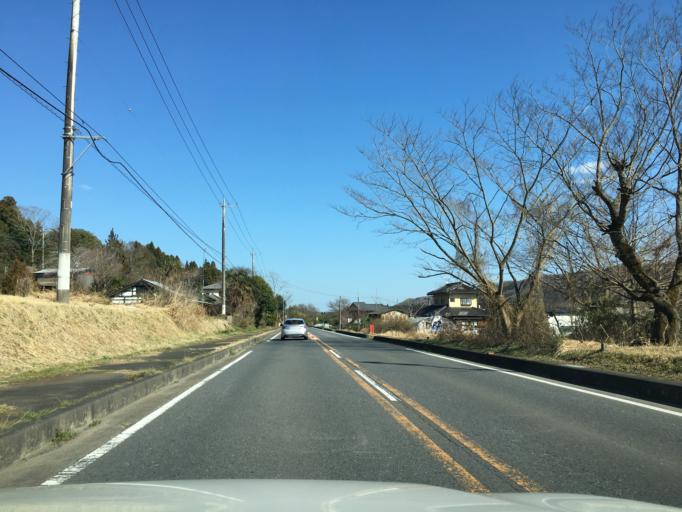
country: JP
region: Tochigi
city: Motegi
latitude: 36.5619
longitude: 140.2572
